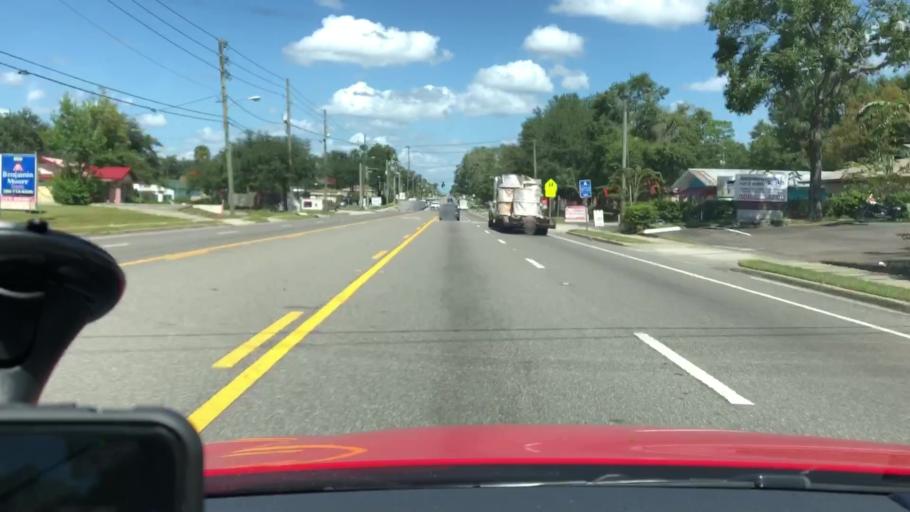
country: US
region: Florida
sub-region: Volusia County
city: Orange City
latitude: 28.9417
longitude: -81.2989
